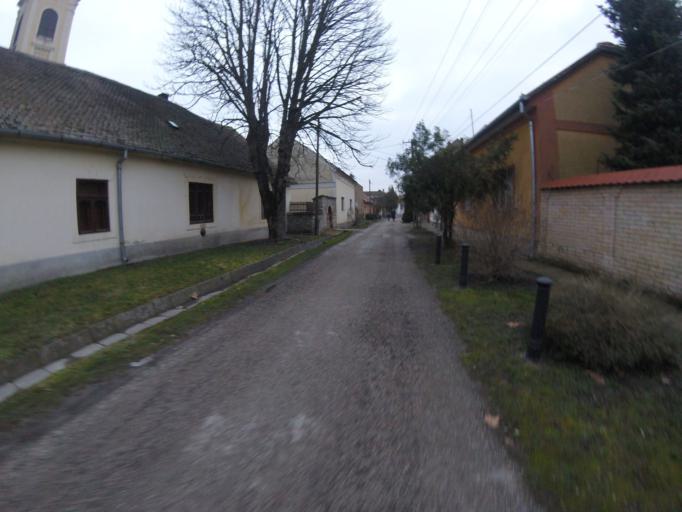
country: HU
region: Baranya
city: Mohacs
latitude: 45.9948
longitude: 18.6901
